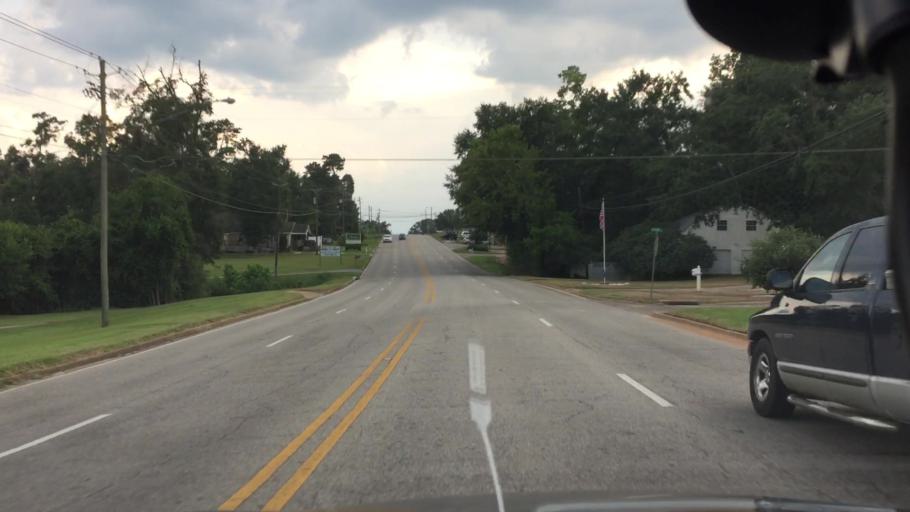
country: US
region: Alabama
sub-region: Coffee County
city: Enterprise
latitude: 31.3231
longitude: -85.8463
